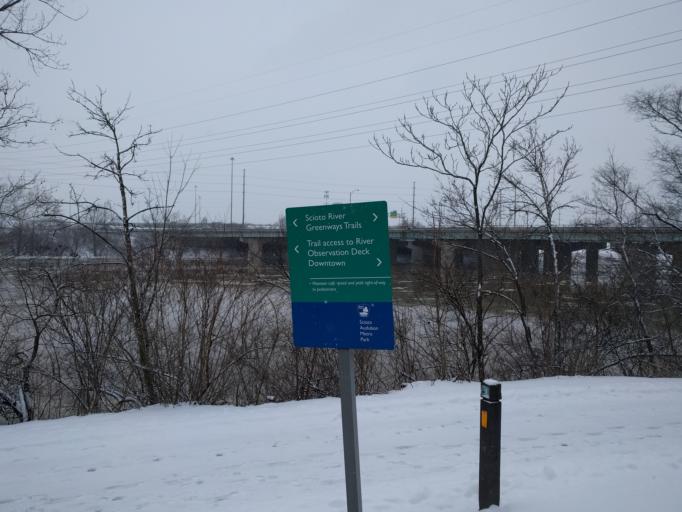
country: US
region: Ohio
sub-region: Franklin County
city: Columbus
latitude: 39.9508
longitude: -83.0119
